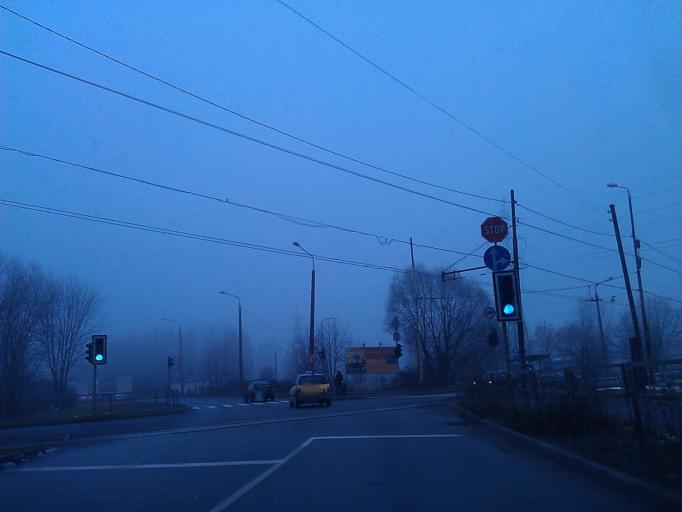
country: LV
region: Riga
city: Riga
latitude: 56.9145
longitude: 24.1228
